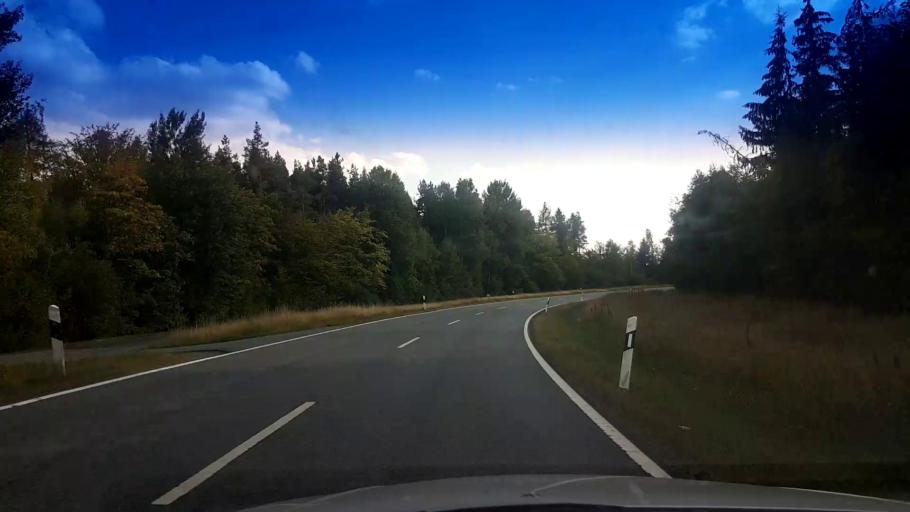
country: DE
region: Bavaria
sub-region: Upper Palatinate
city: Tirschenreuth
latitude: 49.8991
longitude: 12.3769
